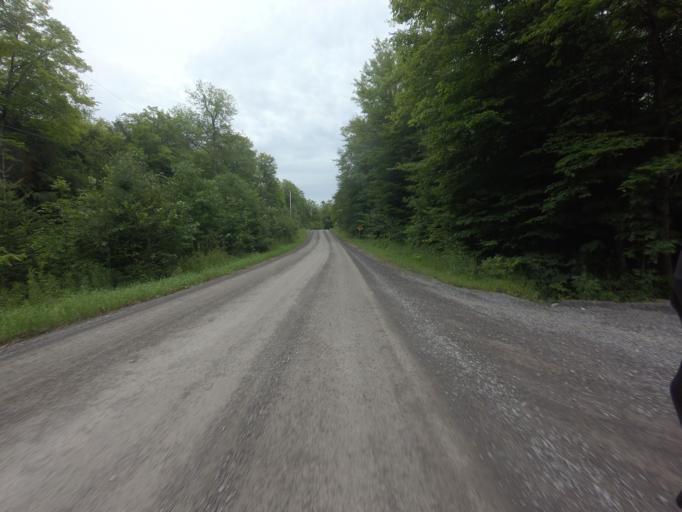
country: CA
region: Ontario
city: Carleton Place
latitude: 45.1507
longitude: -76.2568
